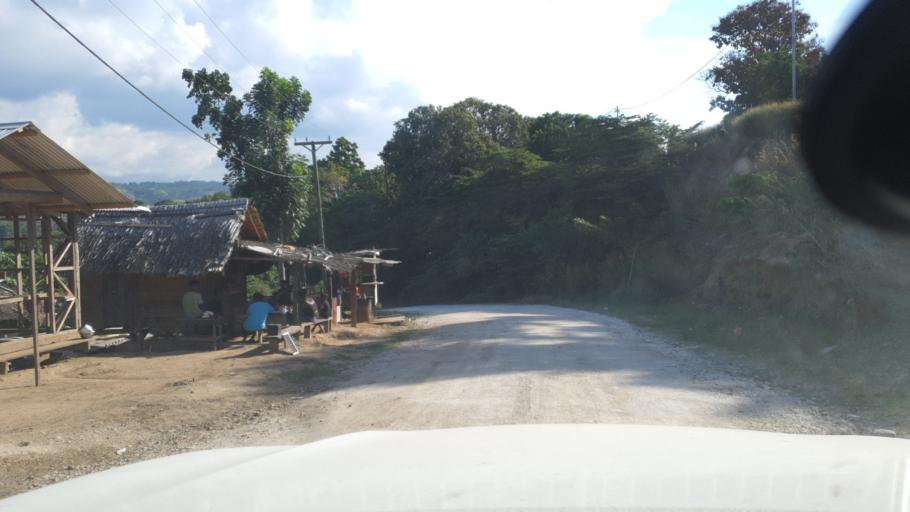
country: SB
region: Guadalcanal
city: Honiara
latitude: -9.4469
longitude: 159.9959
